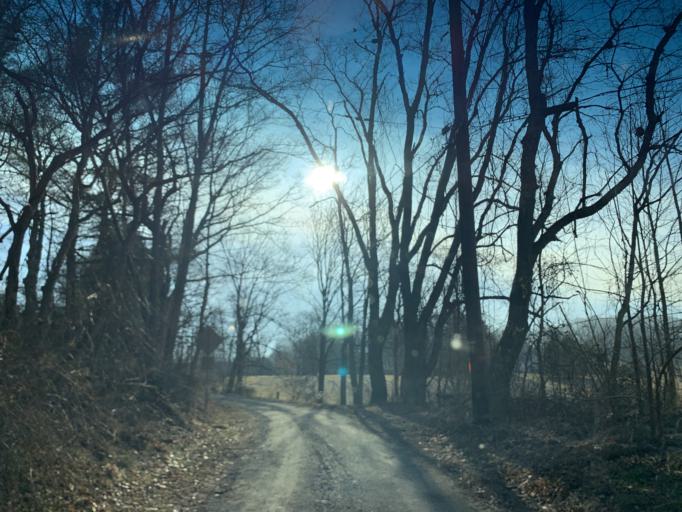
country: US
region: Maryland
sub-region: Harford County
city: Aberdeen
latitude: 39.6107
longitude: -76.2174
